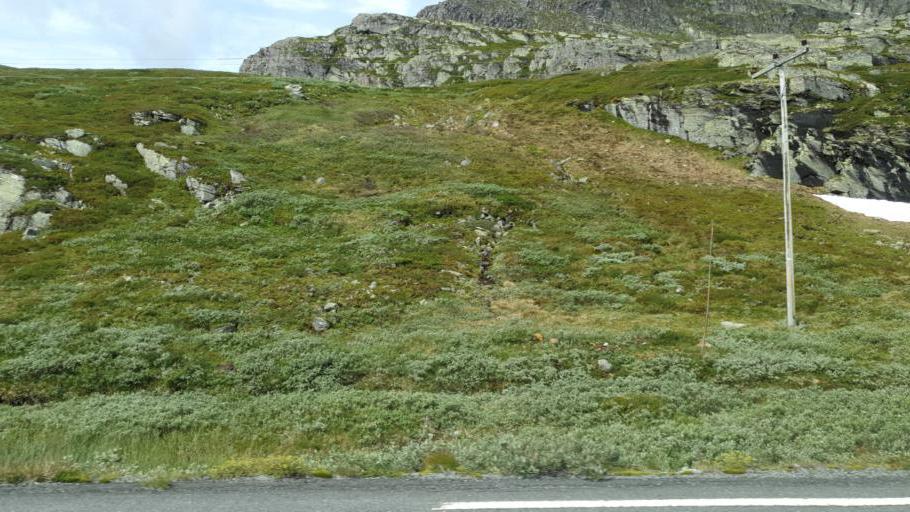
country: NO
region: Oppland
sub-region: Vestre Slidre
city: Slidre
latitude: 61.2915
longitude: 8.8137
